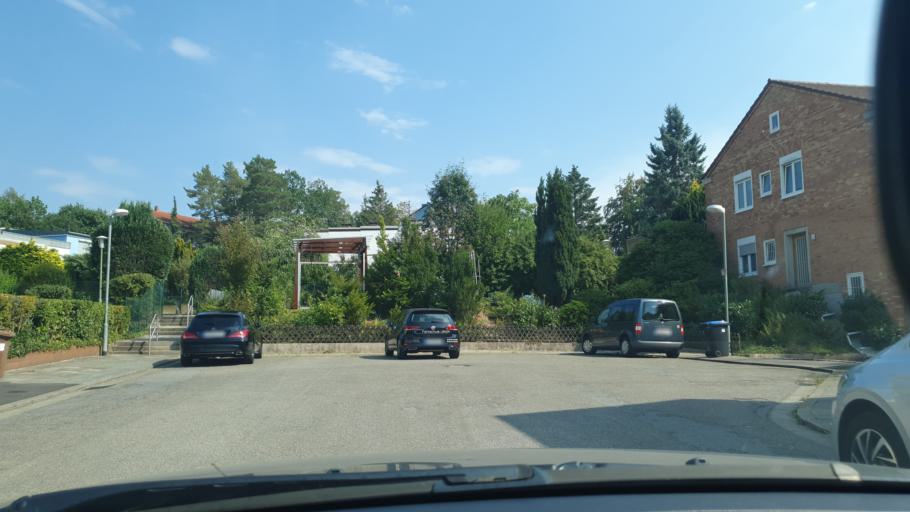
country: DE
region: Rheinland-Pfalz
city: Kaiserslautern
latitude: 49.4337
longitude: 7.7228
